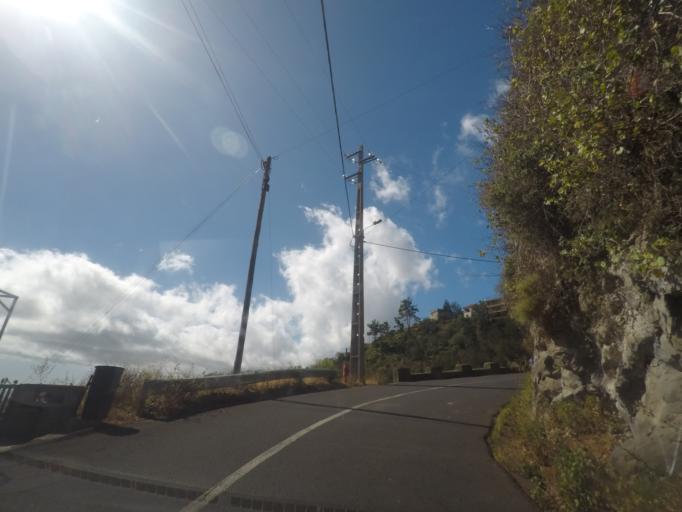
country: PT
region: Madeira
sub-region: Ribeira Brava
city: Campanario
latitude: 32.6901
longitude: -17.0316
